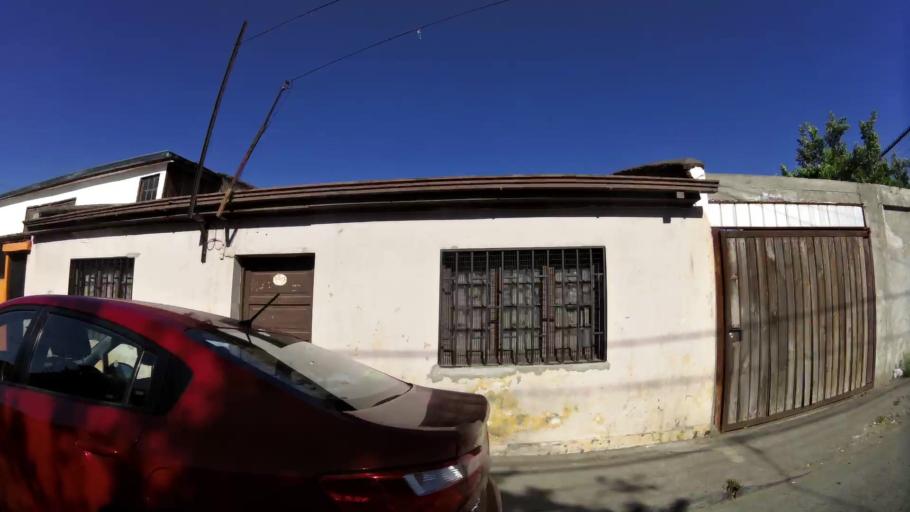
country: CL
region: Santiago Metropolitan
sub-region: Provincia de Maipo
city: San Bernardo
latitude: -33.5488
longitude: -70.6832
